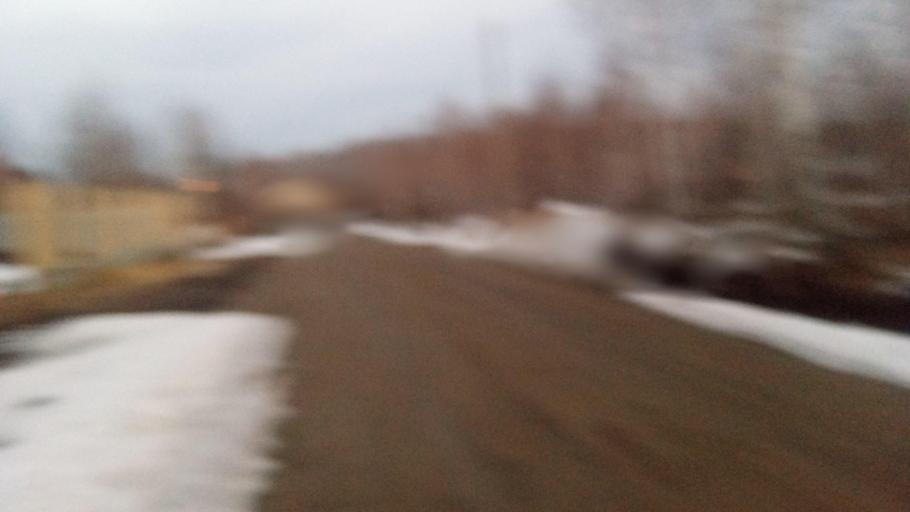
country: RU
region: Chelyabinsk
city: Sargazy
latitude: 55.1020
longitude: 61.2035
